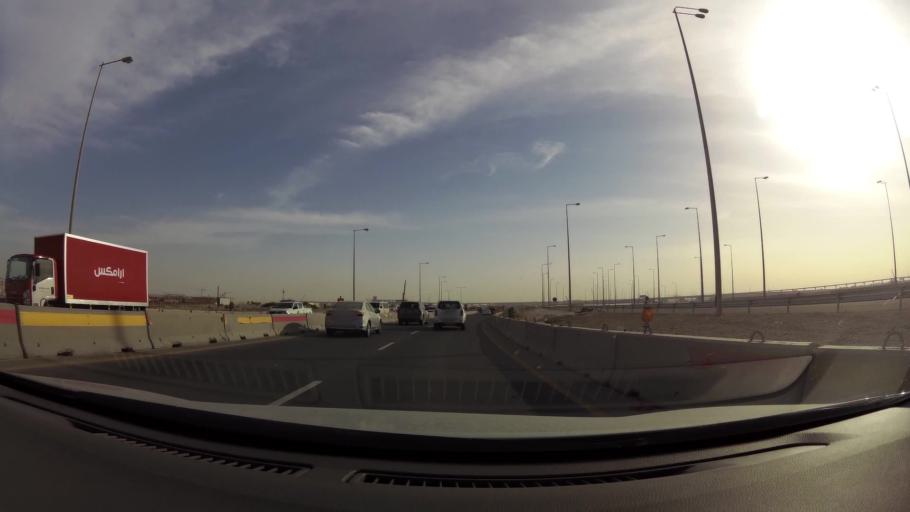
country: QA
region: Al Wakrah
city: Al Wakrah
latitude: 25.2258
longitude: 51.5912
